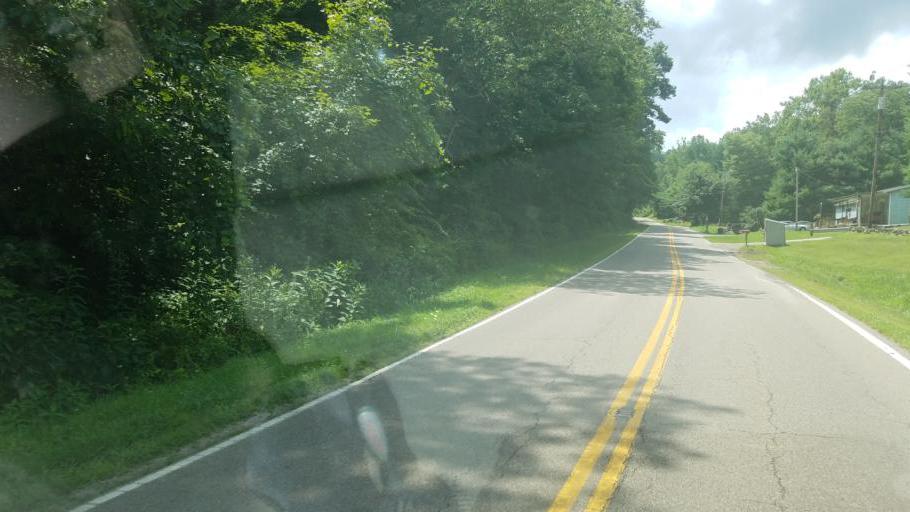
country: US
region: Ohio
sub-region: Ross County
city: Kingston
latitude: 39.4186
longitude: -82.7472
